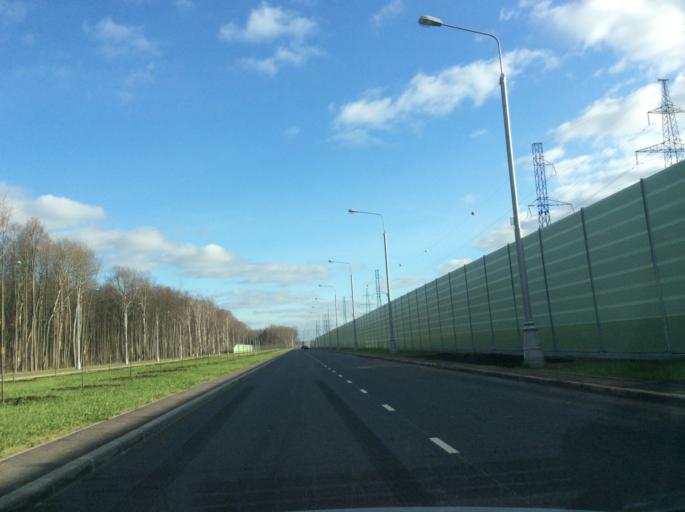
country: RU
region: Moskovskaya
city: Vatutinki
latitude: 55.4826
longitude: 37.3601
